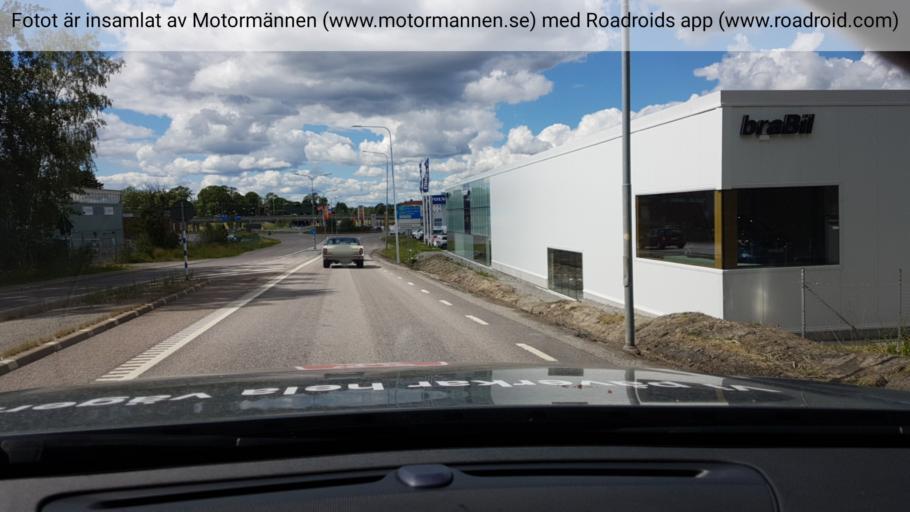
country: SE
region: Stockholm
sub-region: Vallentuna Kommun
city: Vallentuna
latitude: 59.5310
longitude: 18.0849
